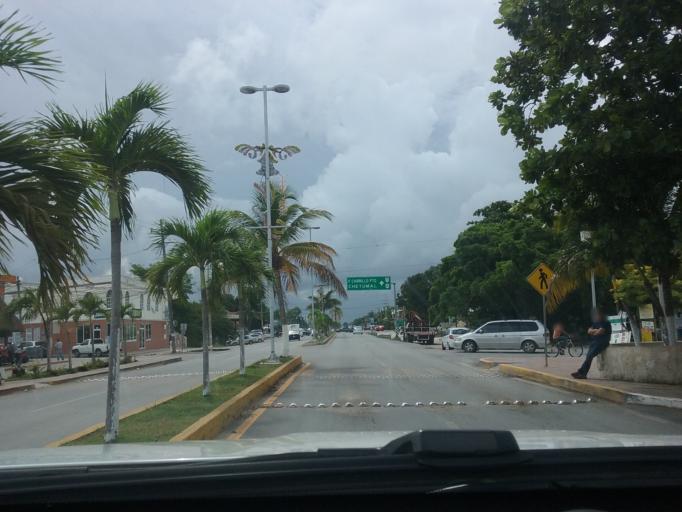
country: MX
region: Quintana Roo
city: Tulum
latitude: 20.2100
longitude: -87.4667
